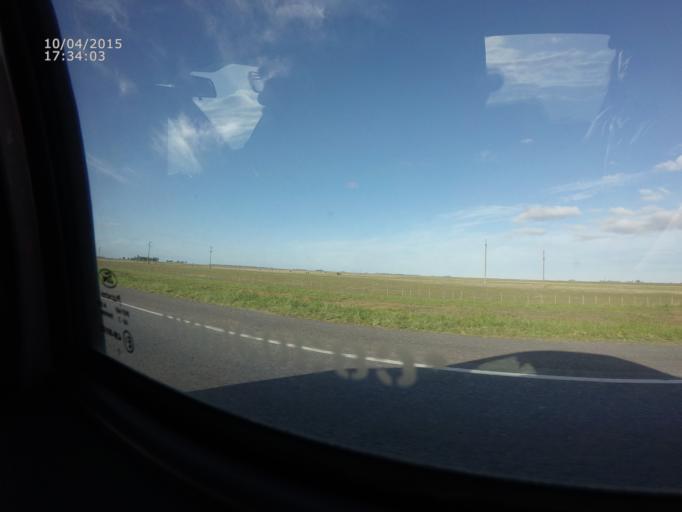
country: AR
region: Buenos Aires
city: Maipu
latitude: -36.9283
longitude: -57.8758
